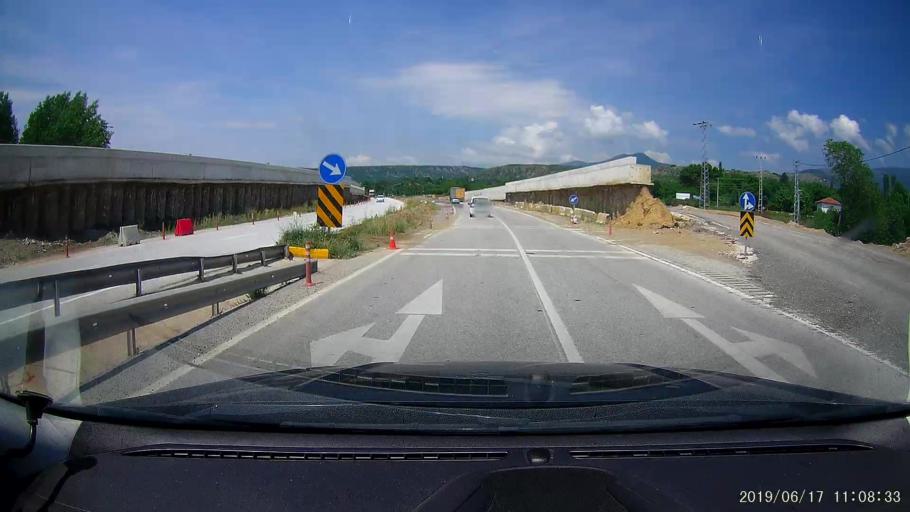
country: TR
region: Kastamonu
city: Tosya
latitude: 41.0005
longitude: 34.0360
